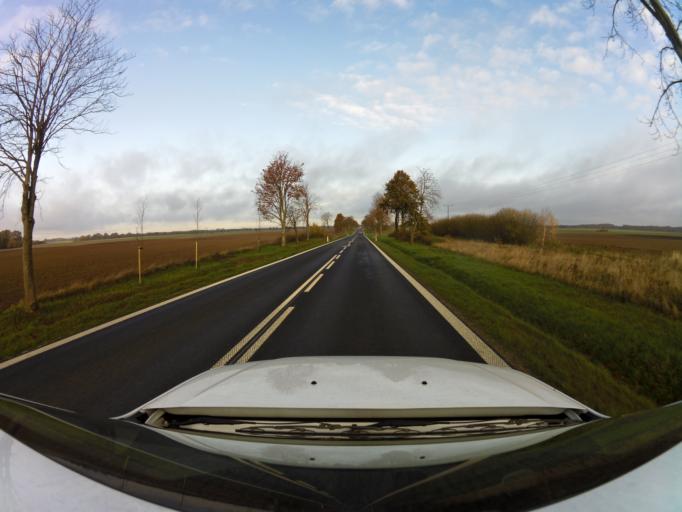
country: PL
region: West Pomeranian Voivodeship
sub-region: Powiat gryficki
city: Ploty
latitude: 53.8335
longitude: 15.2425
